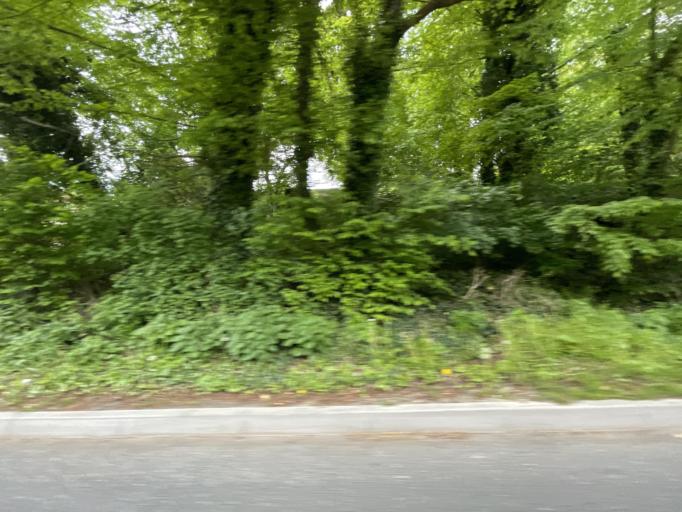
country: HR
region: Grad Zagreb
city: Zagreb - Centar
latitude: 45.8231
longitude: 15.9435
